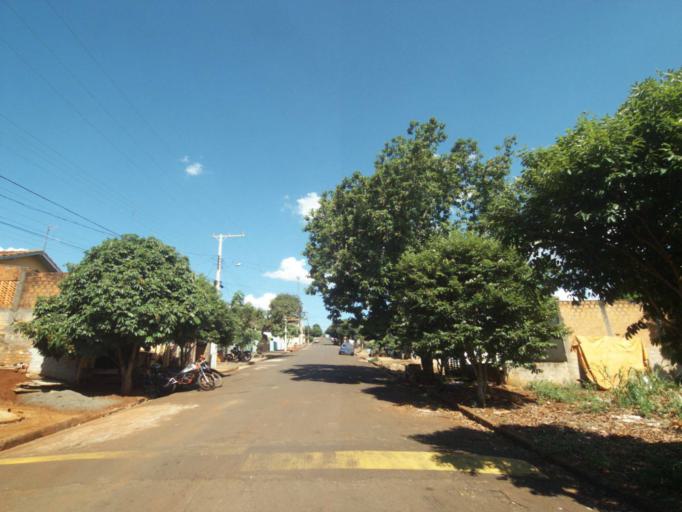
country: BR
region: Parana
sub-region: Sertanopolis
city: Sertanopolis
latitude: -23.0386
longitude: -50.8203
